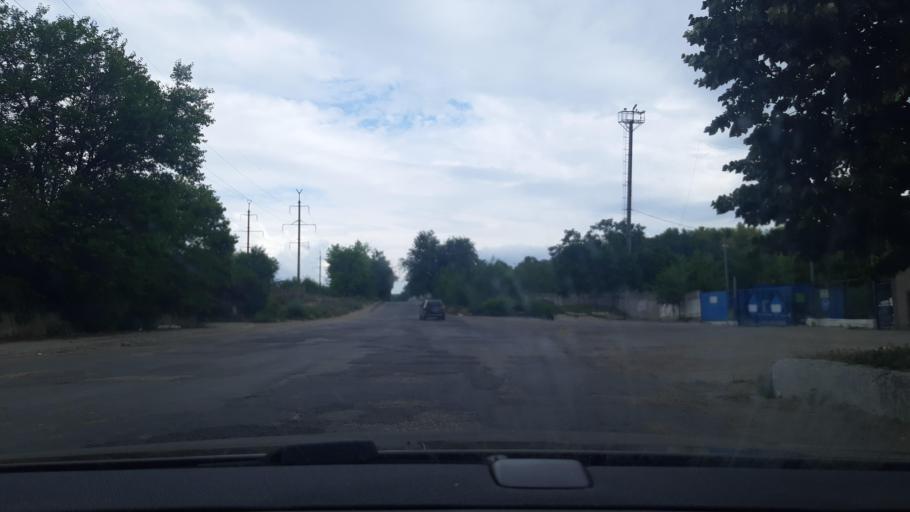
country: MD
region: Chisinau
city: Chisinau
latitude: 46.9973
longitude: 28.9094
